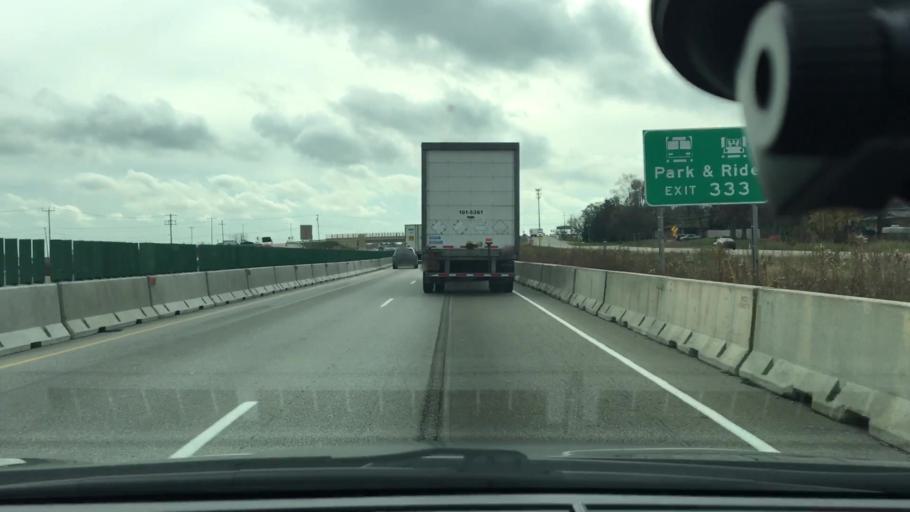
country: US
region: Wisconsin
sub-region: Racine County
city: Franksville
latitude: 42.7373
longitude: -87.9542
